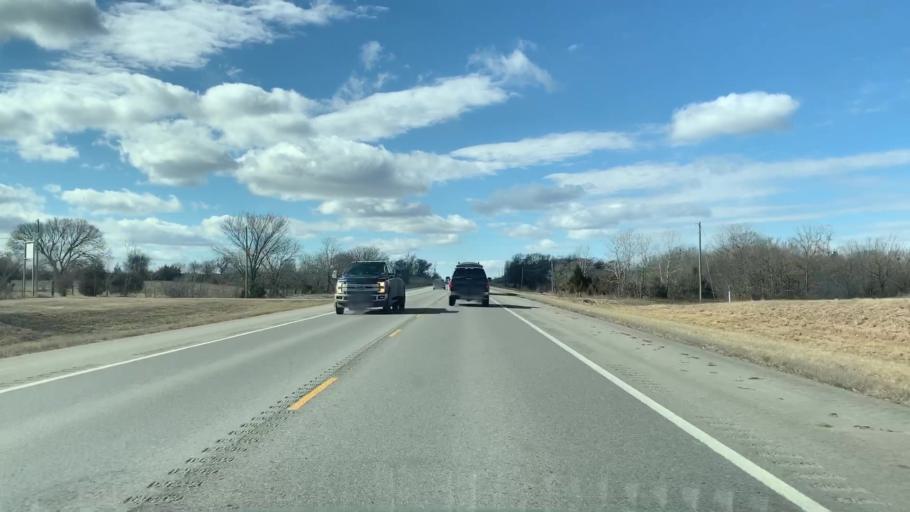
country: US
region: Kansas
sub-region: Cherokee County
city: Columbus
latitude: 37.3399
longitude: -94.8902
